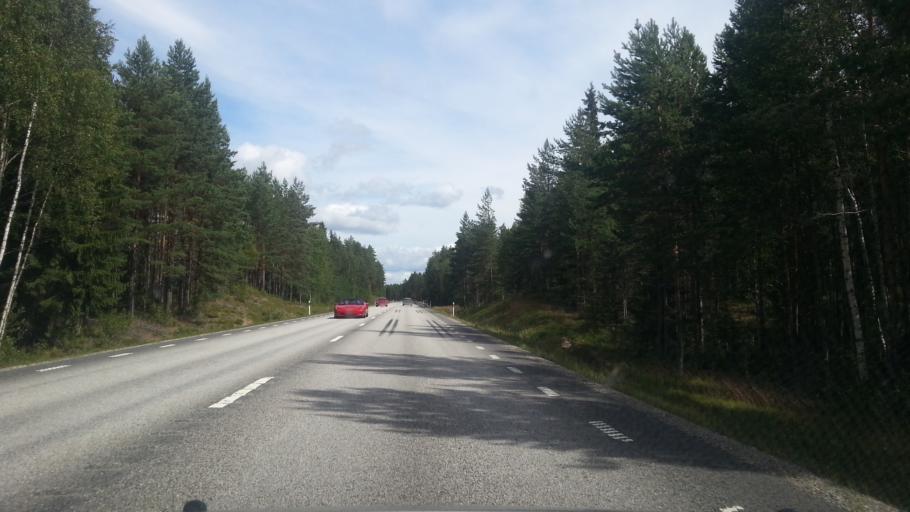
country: SE
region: OErebro
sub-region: Lindesbergs Kommun
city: Lindesberg
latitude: 59.6770
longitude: 15.3062
